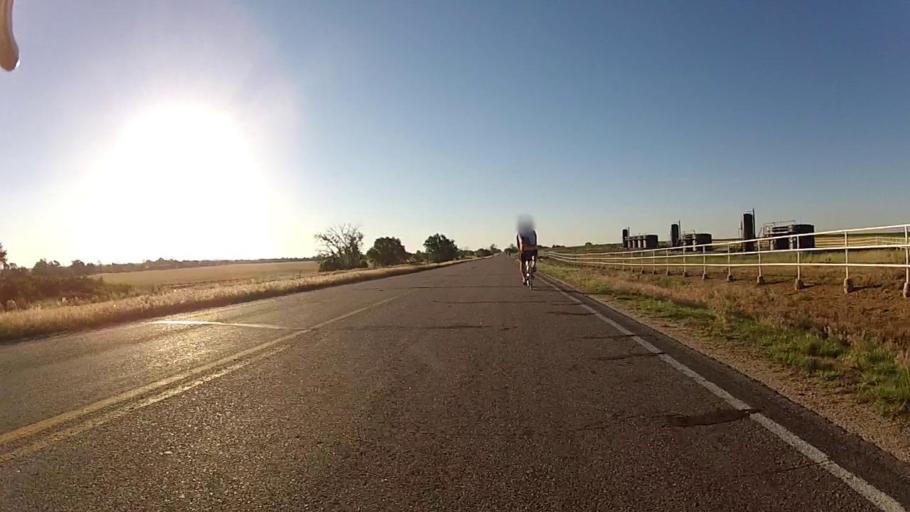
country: US
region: Kansas
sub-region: Ford County
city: Dodge City
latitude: 37.7190
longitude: -99.9456
